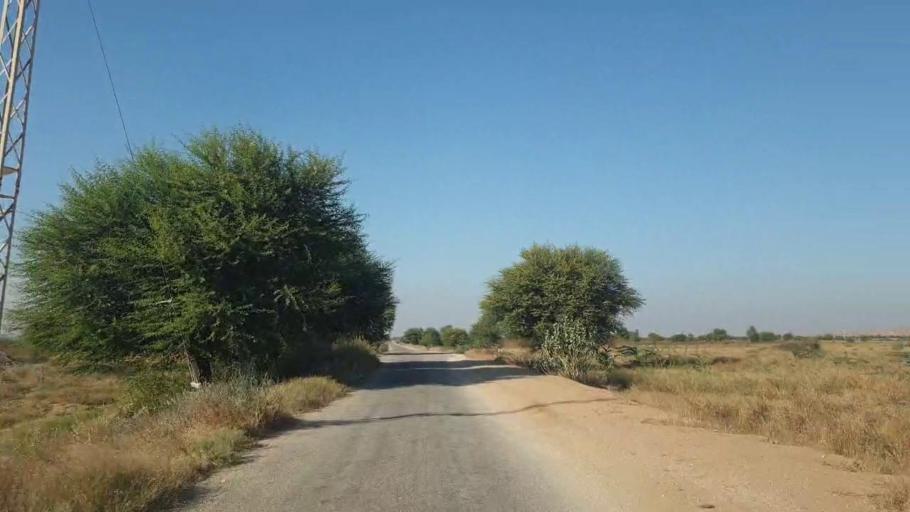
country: PK
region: Sindh
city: Malir Cantonment
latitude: 25.4221
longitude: 67.4620
